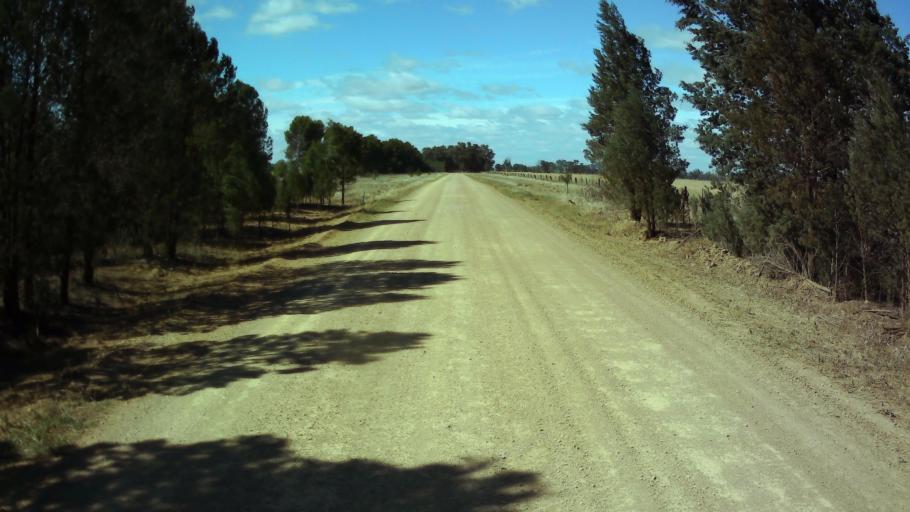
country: AU
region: New South Wales
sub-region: Weddin
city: Grenfell
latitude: -34.0320
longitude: 148.3173
